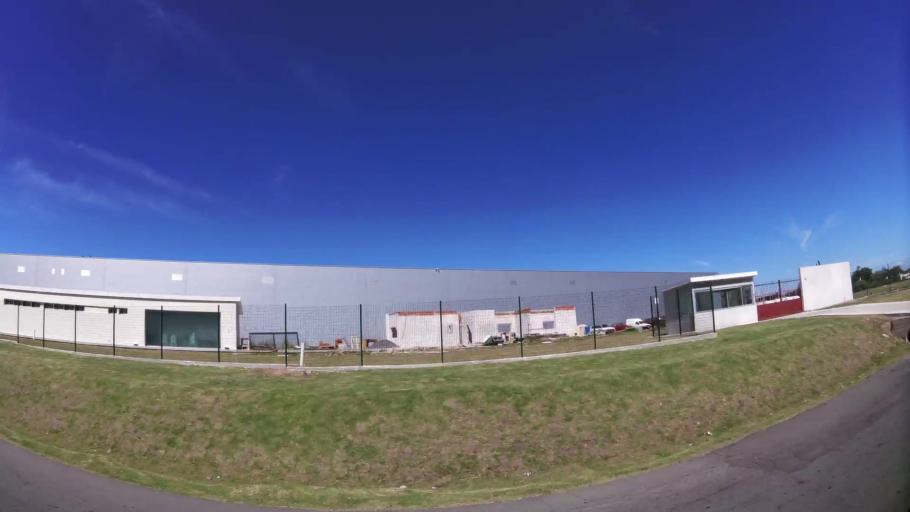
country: UY
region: Canelones
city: Paso de Carrasco
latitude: -34.8640
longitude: -56.1111
